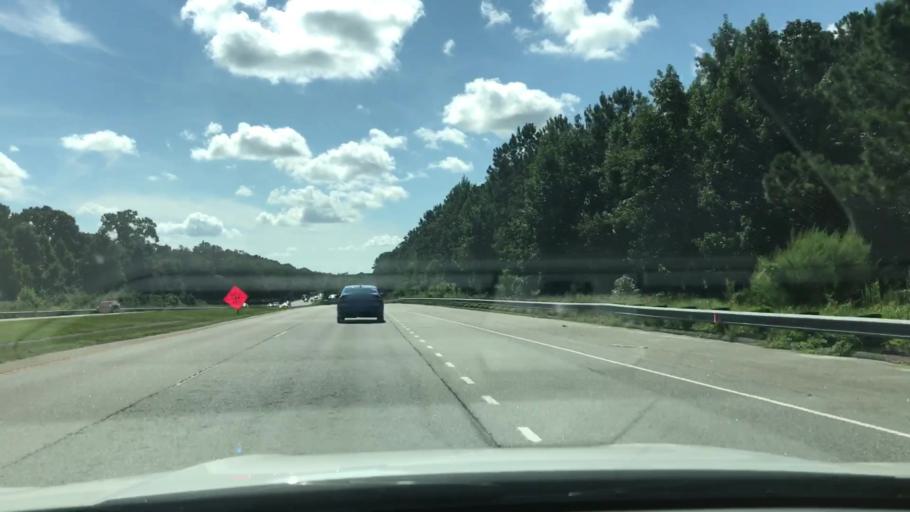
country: US
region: South Carolina
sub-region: Charleston County
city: Shell Point
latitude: 32.8229
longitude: -80.0744
